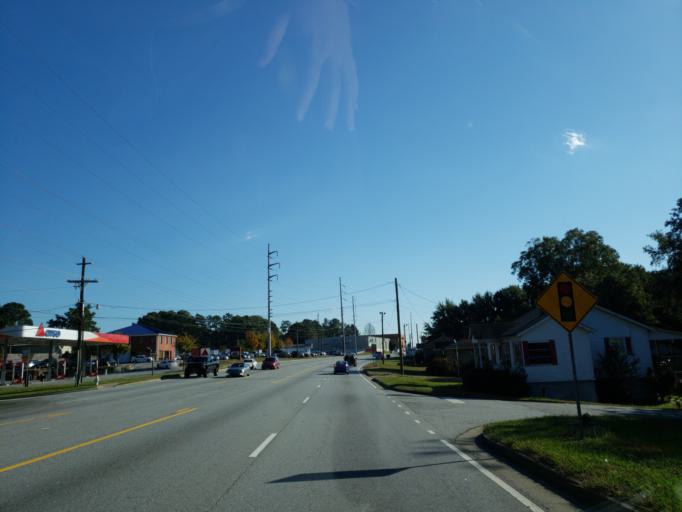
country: US
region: Georgia
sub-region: Gwinnett County
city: Lawrenceville
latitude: 33.9700
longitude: -83.9860
